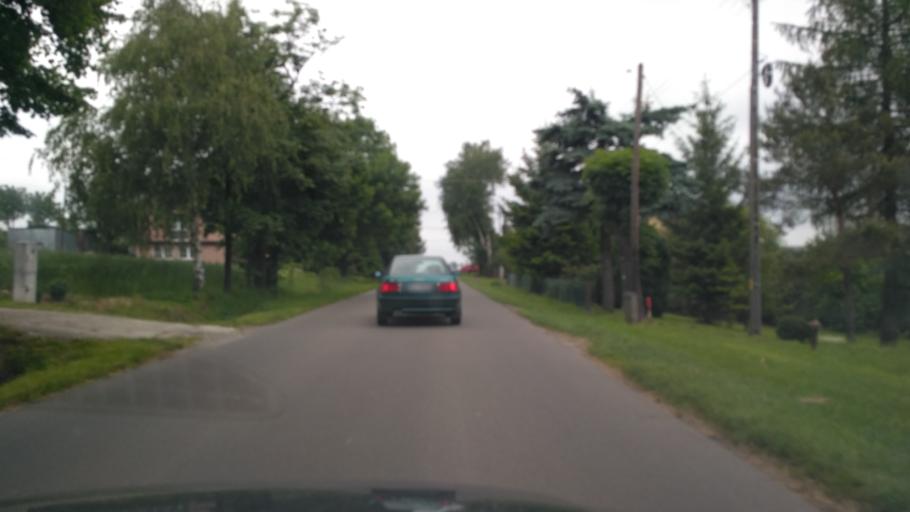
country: PL
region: Subcarpathian Voivodeship
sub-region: Powiat ropczycko-sedziszowski
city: Zagorzyce
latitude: 50.0386
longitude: 21.6970
